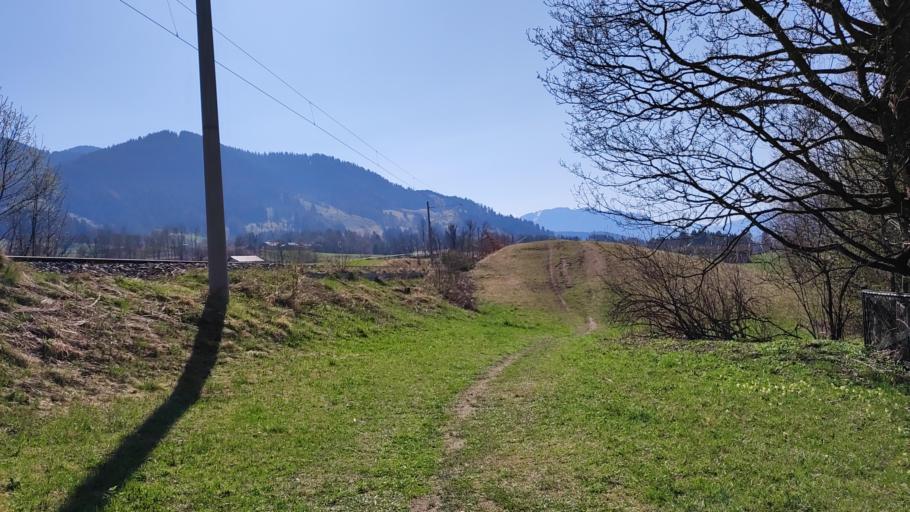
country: DE
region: Bavaria
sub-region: Upper Bavaria
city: Saulgrub
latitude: 47.6459
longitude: 11.0207
